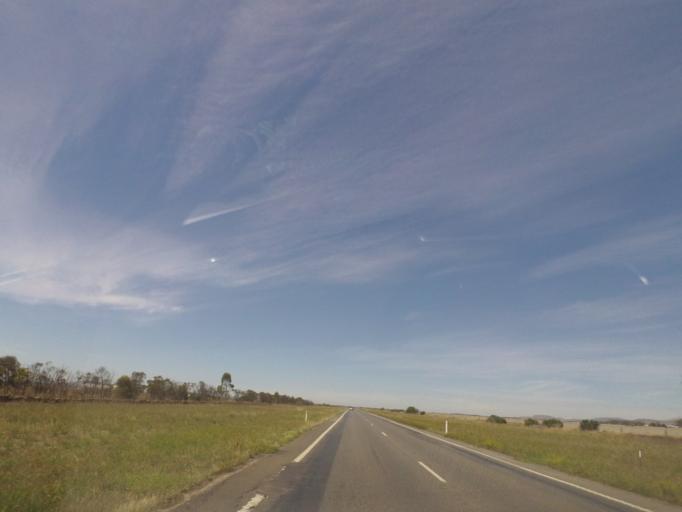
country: AU
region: Victoria
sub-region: Wyndham
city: Wyndham Vale
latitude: -37.8214
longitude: 144.3968
